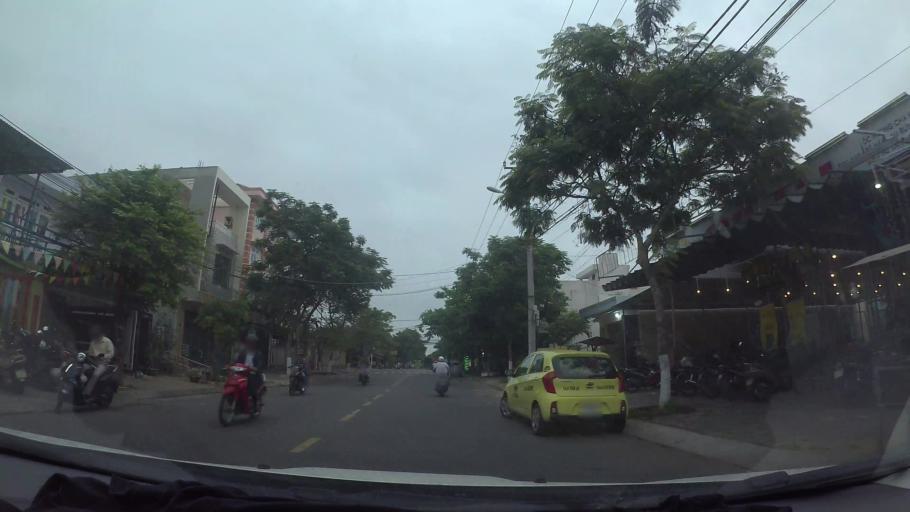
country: VN
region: Da Nang
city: Lien Chieu
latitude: 16.0735
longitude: 108.1575
